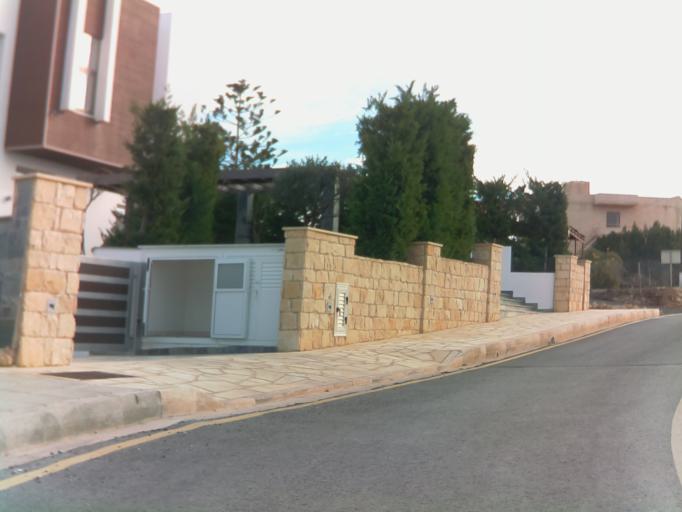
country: CY
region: Pafos
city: Pegeia
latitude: 34.9032
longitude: 32.3207
